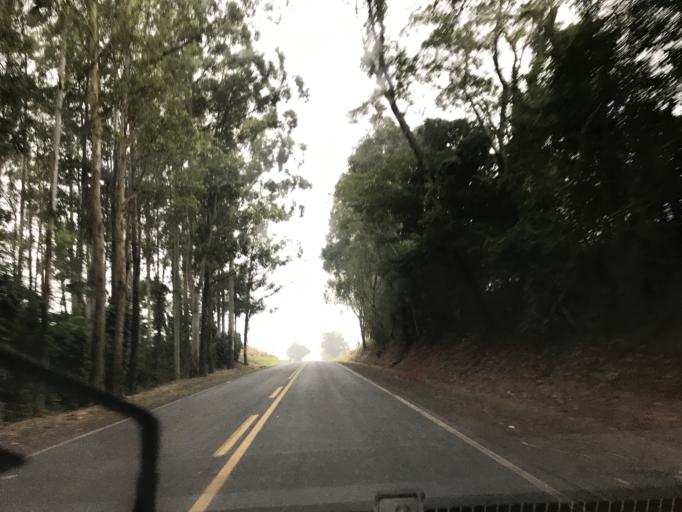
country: PY
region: Canindeyu
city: Salto del Guaira
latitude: -24.1177
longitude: -54.1163
